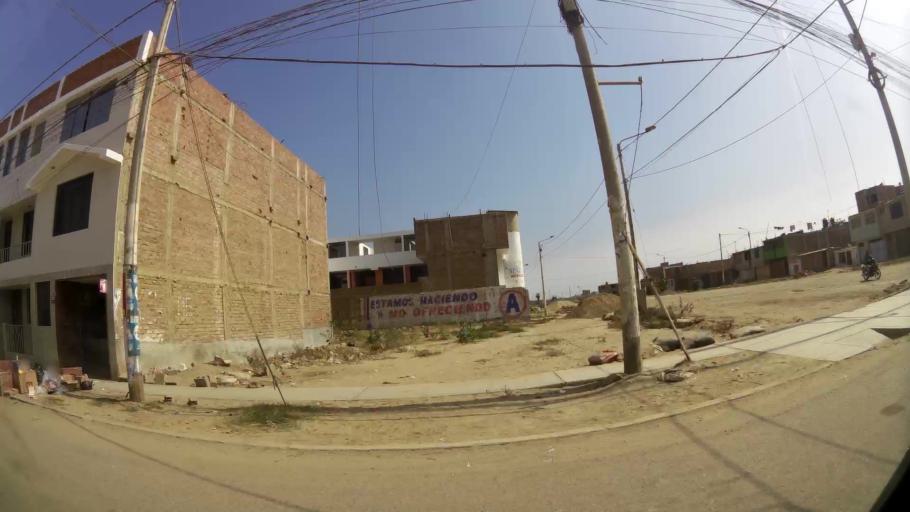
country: PE
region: La Libertad
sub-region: Provincia de Trujillo
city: Buenos Aires
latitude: -8.1345
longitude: -79.0529
